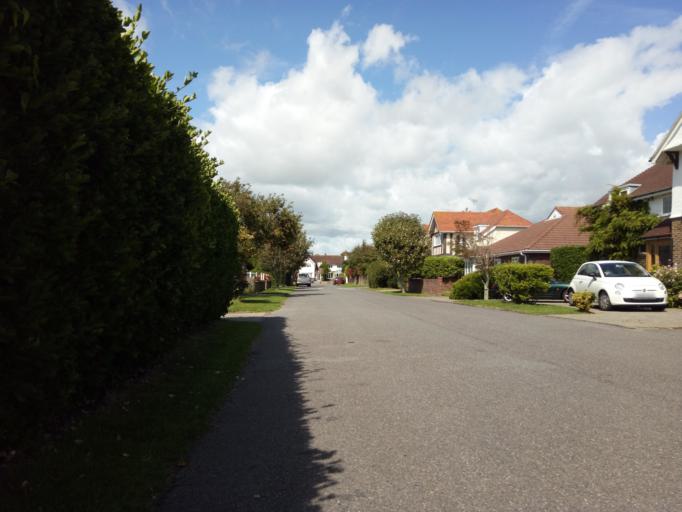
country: GB
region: England
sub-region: West Sussex
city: Bognor Regis
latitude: 50.7887
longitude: -0.6422
